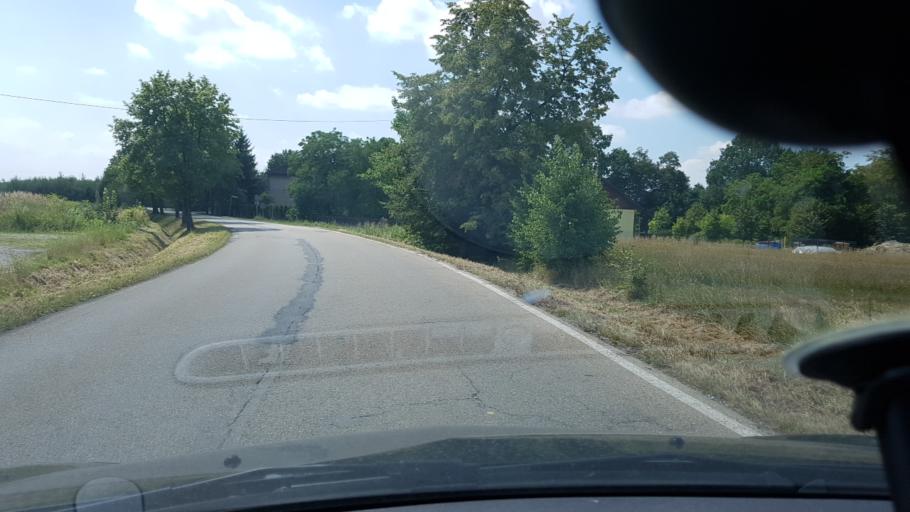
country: PL
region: Lesser Poland Voivodeship
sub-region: Powiat oswiecimski
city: Brzezinka
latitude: 50.0530
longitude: 19.1873
